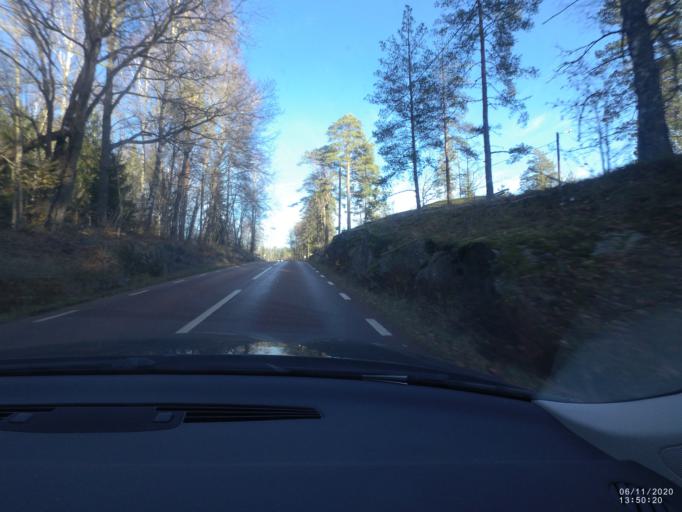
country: SE
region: Soedermanland
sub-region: Nykopings Kommun
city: Nykoping
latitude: 58.9295
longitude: 17.1056
